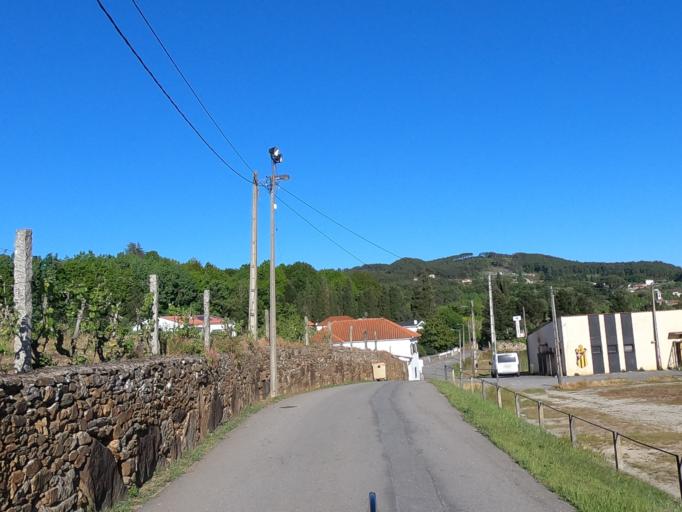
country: PT
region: Vila Real
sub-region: Vila Real
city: Vila Real
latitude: 41.2968
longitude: -7.7165
